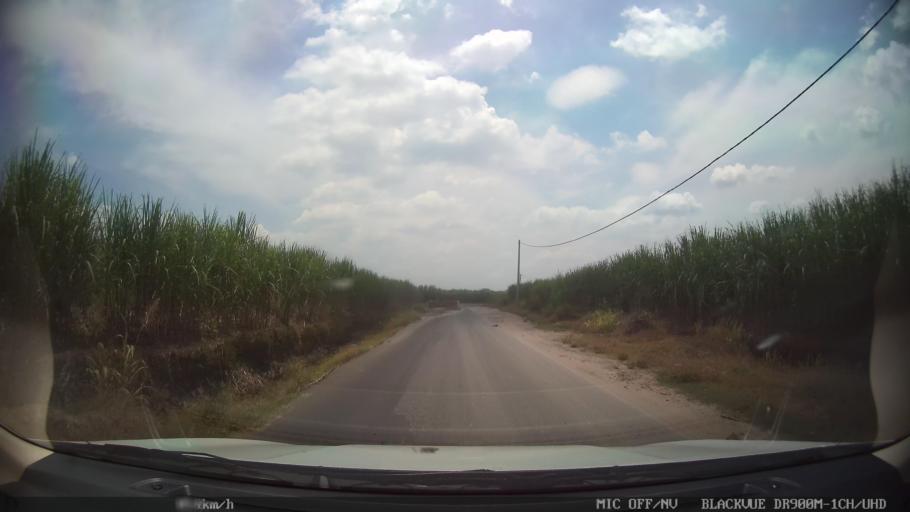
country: ID
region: North Sumatra
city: Binjai
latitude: 3.5928
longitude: 98.5400
